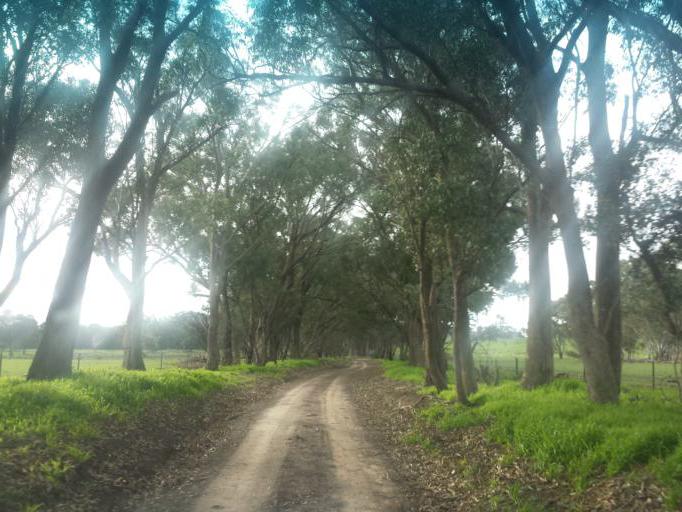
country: AU
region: Victoria
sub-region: Murrindindi
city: Kinglake West
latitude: -37.0207
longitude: 145.2502
